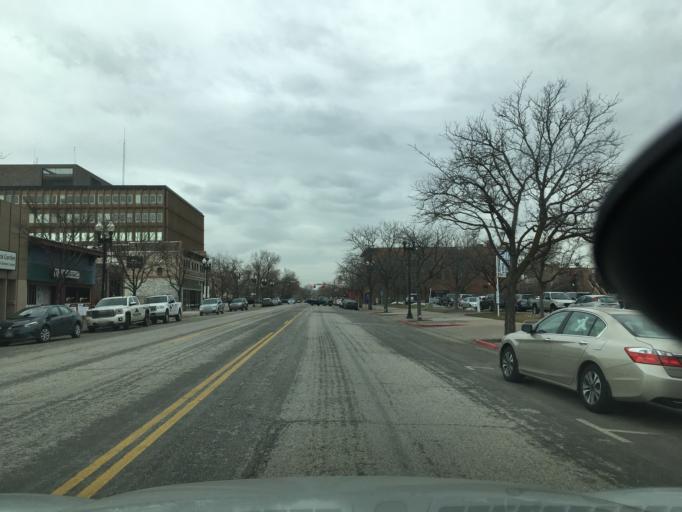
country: US
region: Utah
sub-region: Weber County
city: Ogden
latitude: 41.2224
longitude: -111.9733
